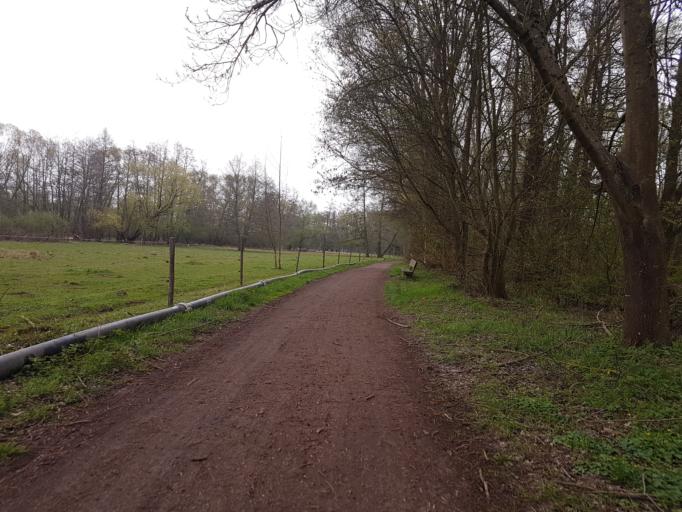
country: DE
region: Rheinland-Pfalz
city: Landau in der Pfalz
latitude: 49.2017
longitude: 8.0924
